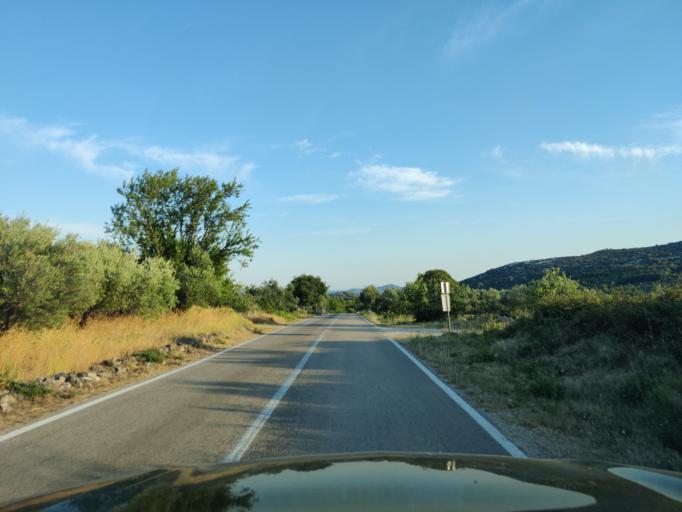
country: HR
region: Sibensko-Kniniska
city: Tribunj
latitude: 43.7788
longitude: 15.7279
